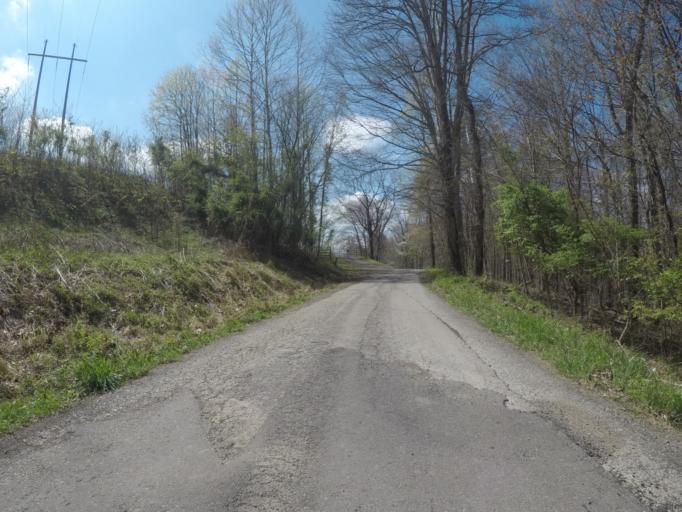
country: US
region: West Virginia
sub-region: Wayne County
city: Ceredo
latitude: 38.3874
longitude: -82.5420
